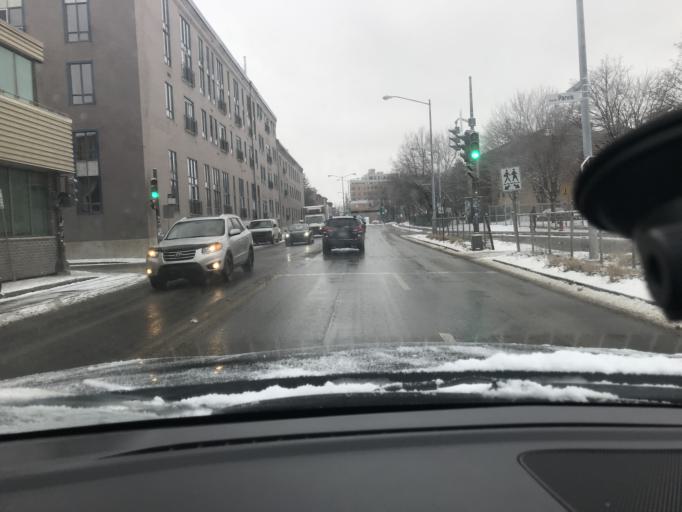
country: CA
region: Quebec
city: Quebec
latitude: 46.8170
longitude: -71.2248
